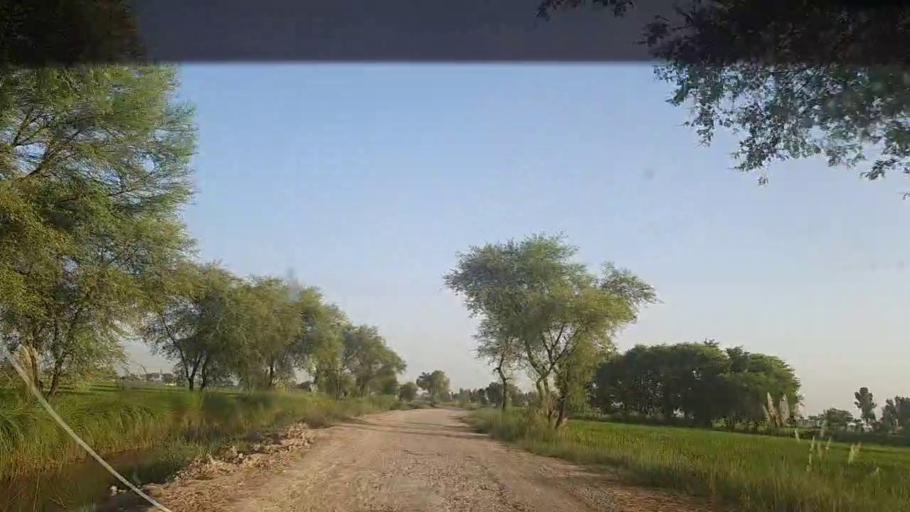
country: PK
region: Sindh
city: Thul
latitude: 28.1249
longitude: 68.8938
